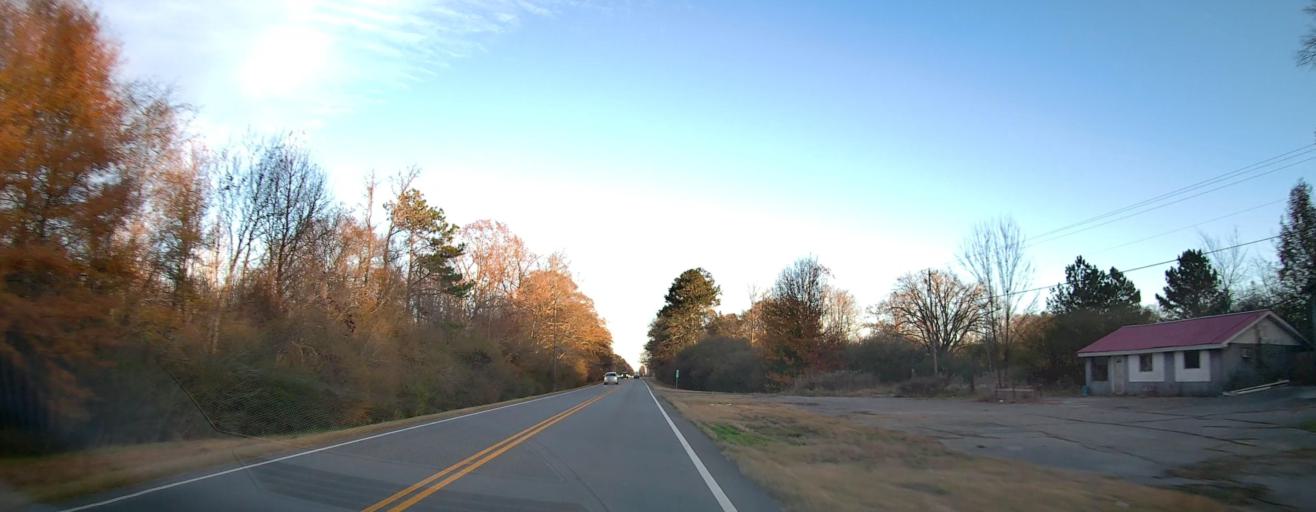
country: US
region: Alabama
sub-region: Saint Clair County
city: Steele
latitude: 34.0550
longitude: -86.2056
